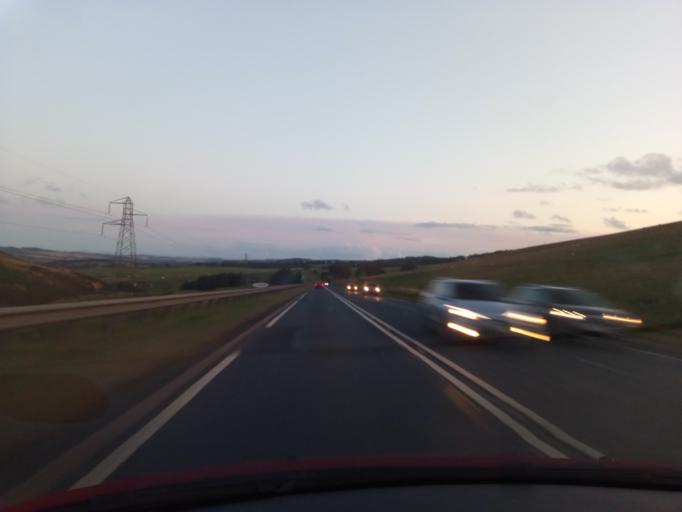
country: GB
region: Scotland
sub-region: The Scottish Borders
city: Lauder
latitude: 55.7954
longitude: -2.8342
